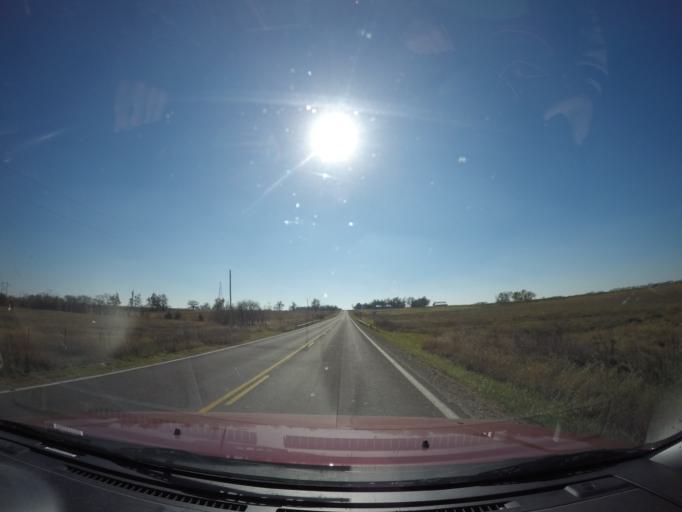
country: US
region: Kansas
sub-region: Morris County
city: Council Grove
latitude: 38.8080
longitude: -96.5014
